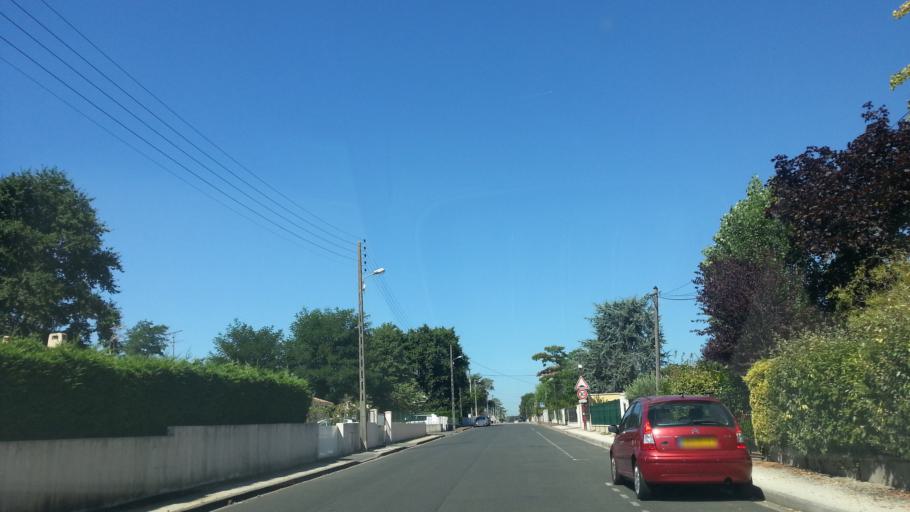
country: FR
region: Aquitaine
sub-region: Departement de la Gironde
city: Villenave-d'Ornon
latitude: 44.7646
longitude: -0.5690
